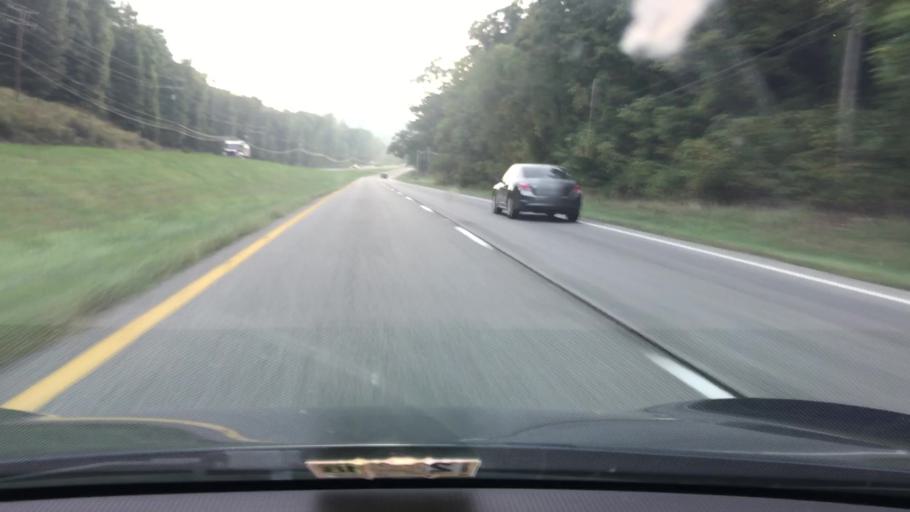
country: US
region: Virginia
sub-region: Botetourt County
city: Blue Ridge
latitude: 37.3968
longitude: -79.7650
